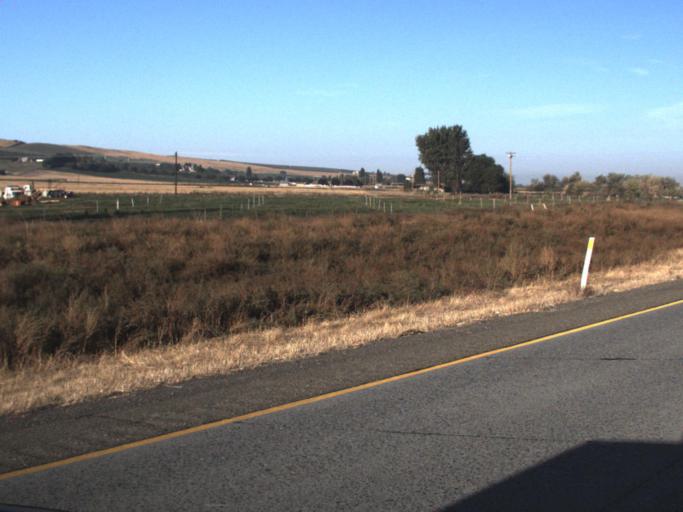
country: US
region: Washington
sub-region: Yakima County
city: Sunnyside
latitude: 46.3198
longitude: -120.0591
